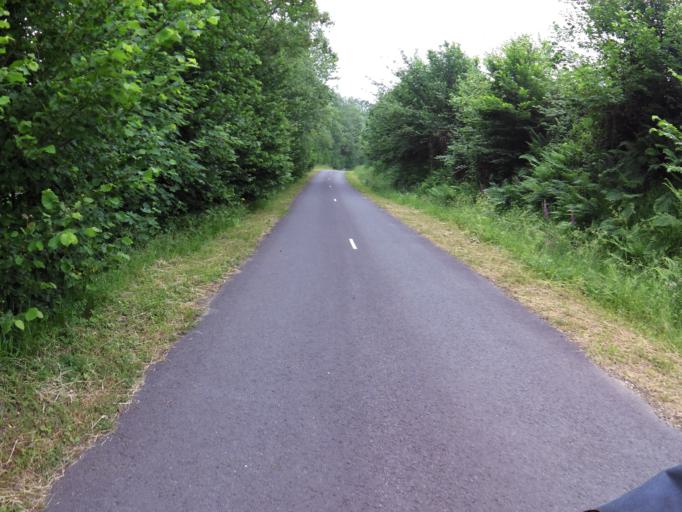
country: FR
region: Champagne-Ardenne
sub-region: Departement des Ardennes
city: Fumay
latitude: 49.9793
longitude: 4.6731
